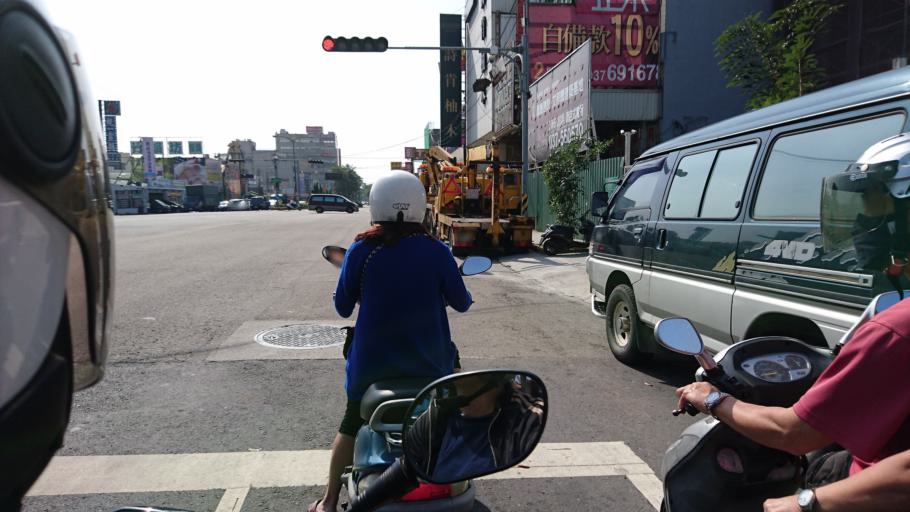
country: TW
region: Taiwan
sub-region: Hsinchu
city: Hsinchu
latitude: 24.6935
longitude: 120.9149
